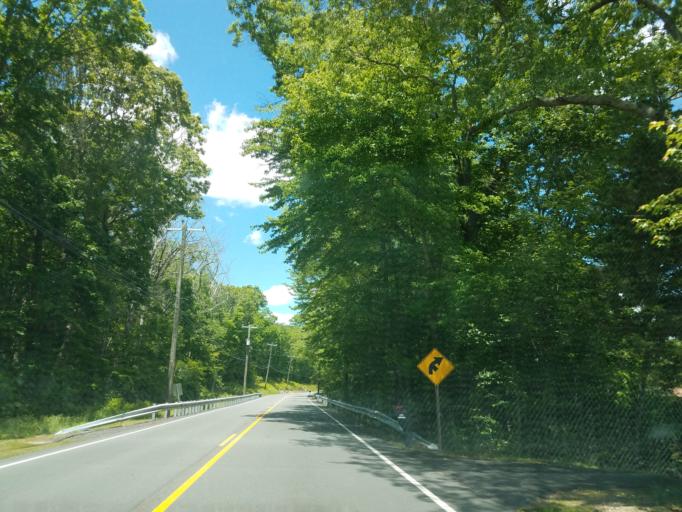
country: US
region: Connecticut
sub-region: New London County
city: Niantic
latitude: 41.4082
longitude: -72.2256
